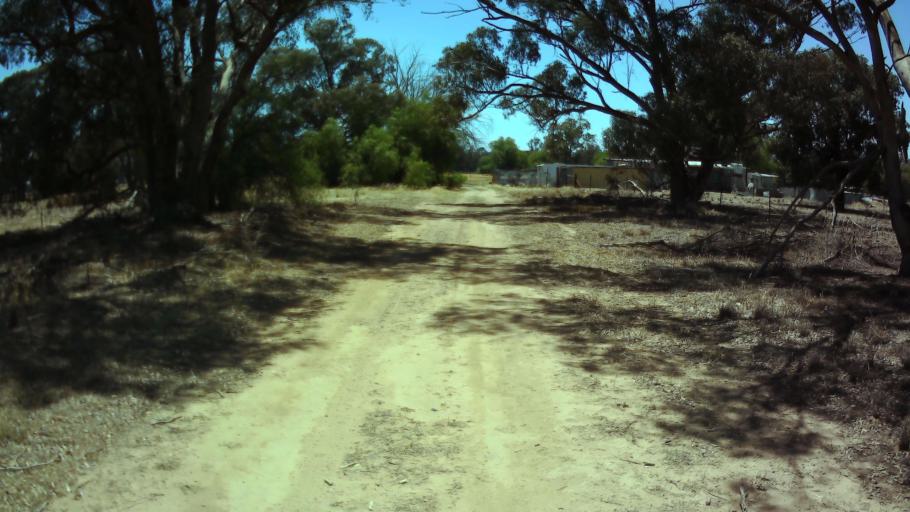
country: AU
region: New South Wales
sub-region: Weddin
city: Grenfell
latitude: -34.0361
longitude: 147.9282
